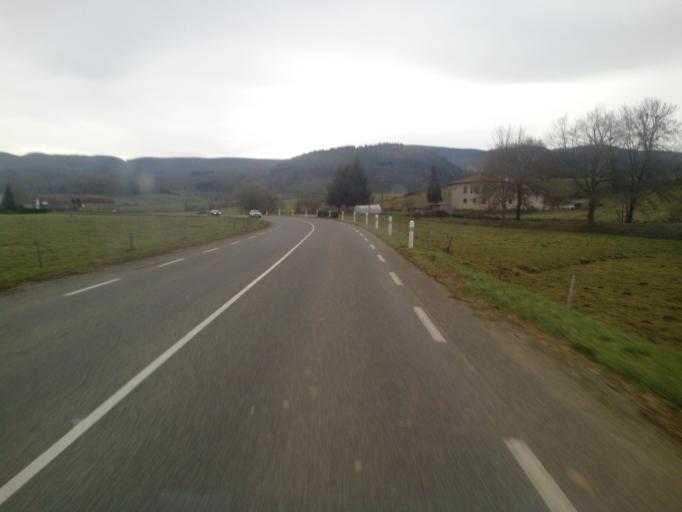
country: FR
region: Midi-Pyrenees
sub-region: Departement de l'Ariege
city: Foix
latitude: 43.0149
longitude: 1.4057
